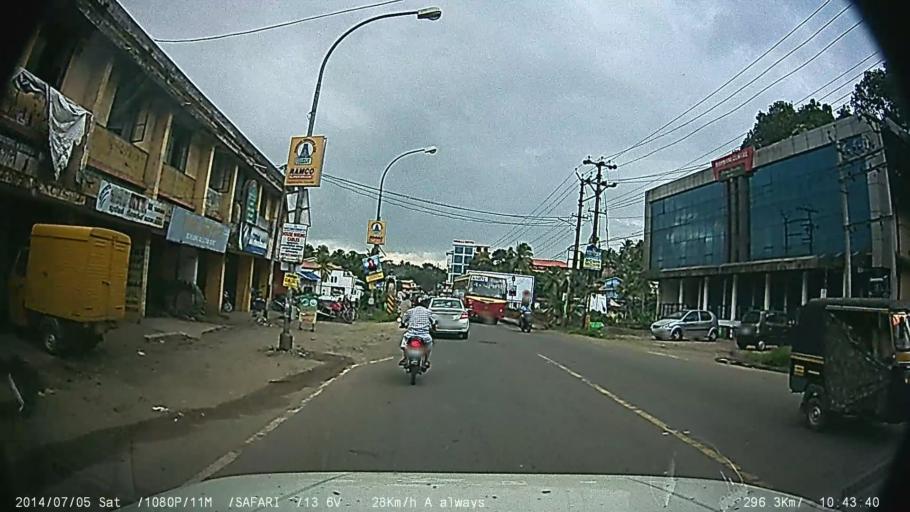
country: IN
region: Kerala
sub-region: Ernakulam
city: Muvattupula
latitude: 9.9793
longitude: 76.5825
